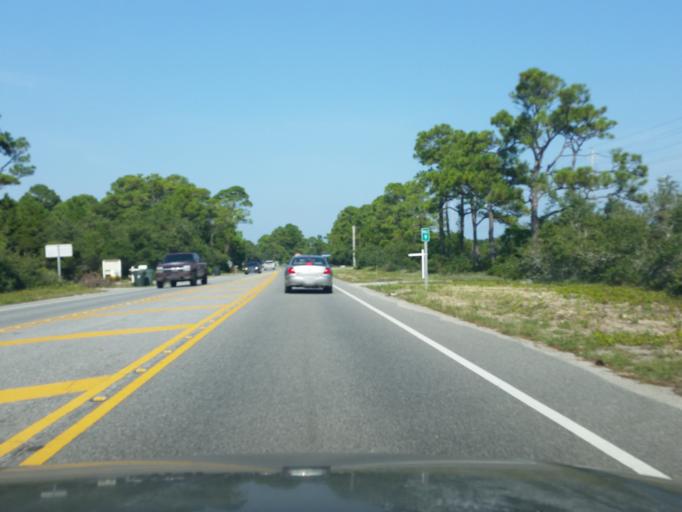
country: US
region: Alabama
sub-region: Baldwin County
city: Gulf Shores
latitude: 30.2380
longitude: -87.8749
